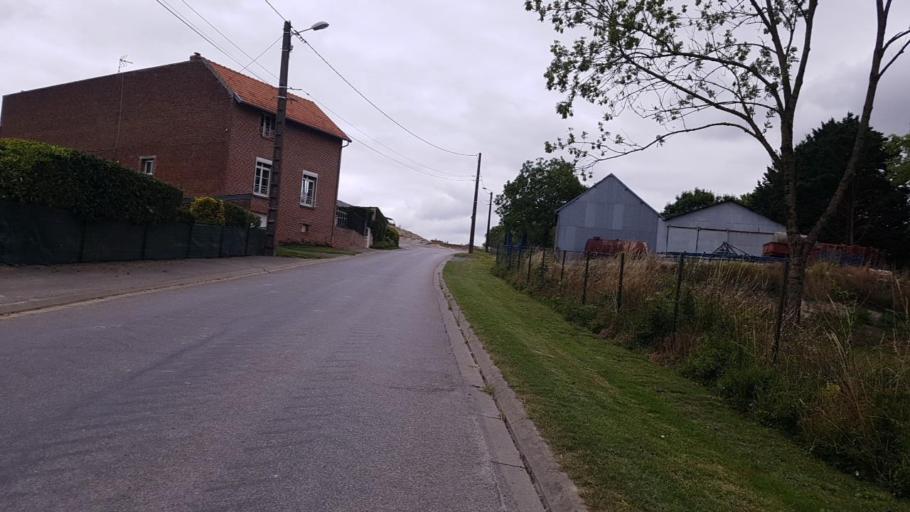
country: FR
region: Picardie
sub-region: Departement de l'Aisne
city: Guise
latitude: 49.8852
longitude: 3.5591
